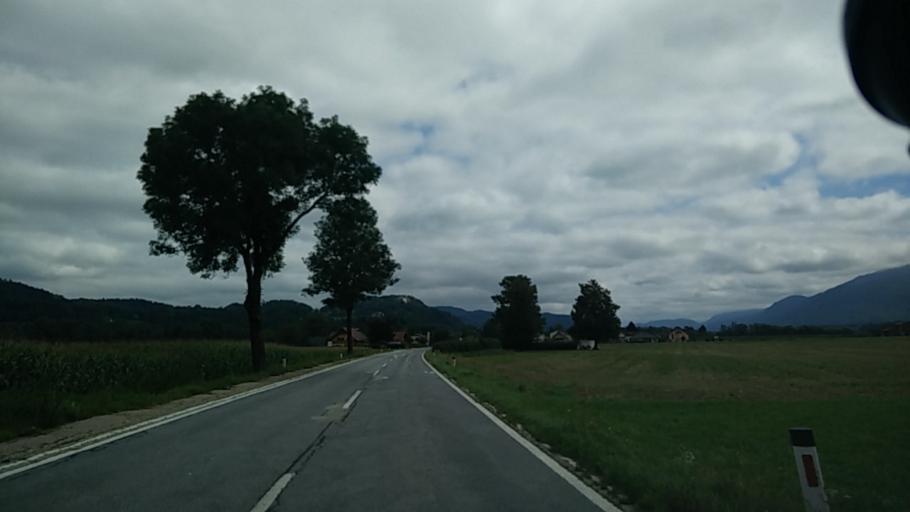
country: AT
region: Carinthia
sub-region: Politischer Bezirk Klagenfurt Land
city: Kottmannsdorf
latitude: 46.5383
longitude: 14.2314
